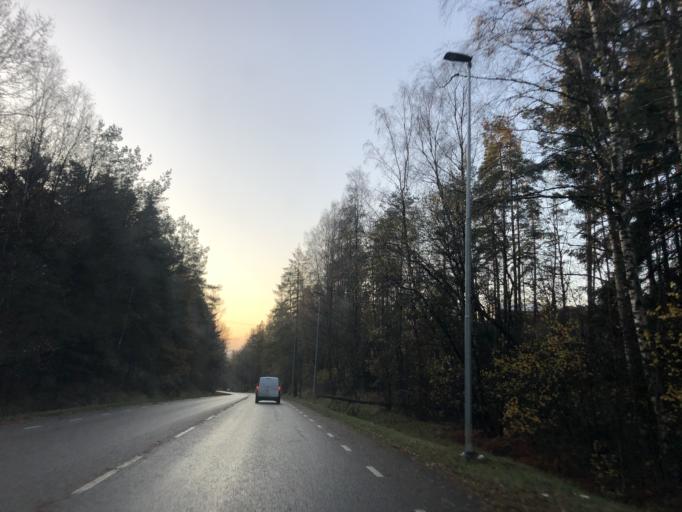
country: SE
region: Vaestra Goetaland
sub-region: Goteborg
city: Gardsten
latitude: 57.7961
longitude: 12.0297
